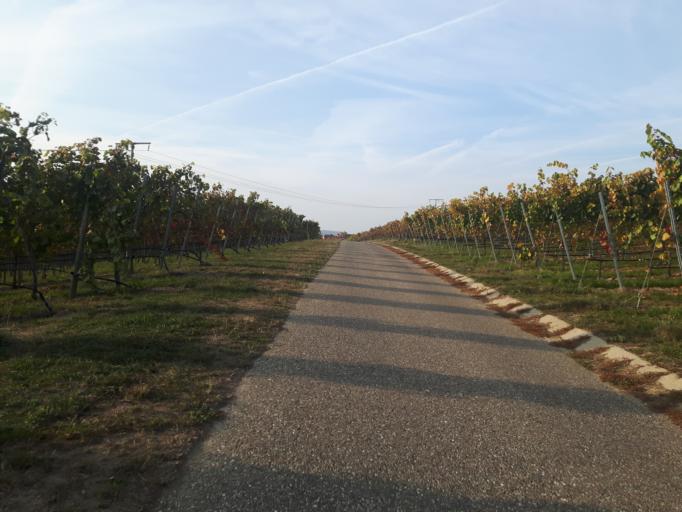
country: DE
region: Baden-Wuerttemberg
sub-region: Regierungsbezirk Stuttgart
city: Talheim
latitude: 49.0710
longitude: 9.1735
